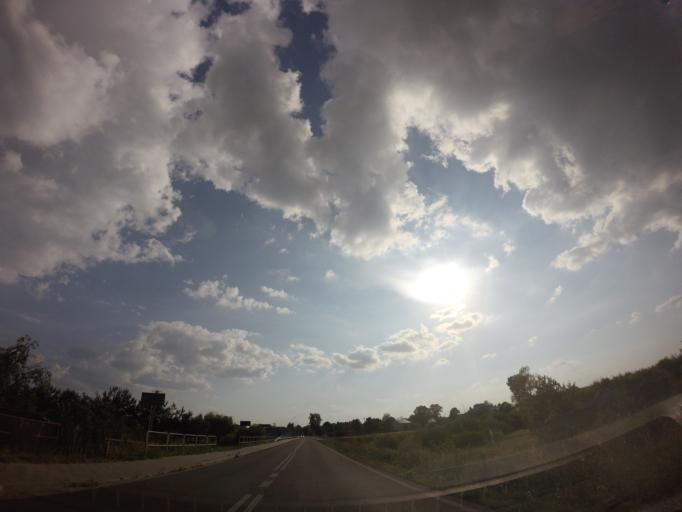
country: PL
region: Lublin Voivodeship
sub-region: Powiat lukowski
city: Wojcieszkow
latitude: 51.8470
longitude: 22.3426
